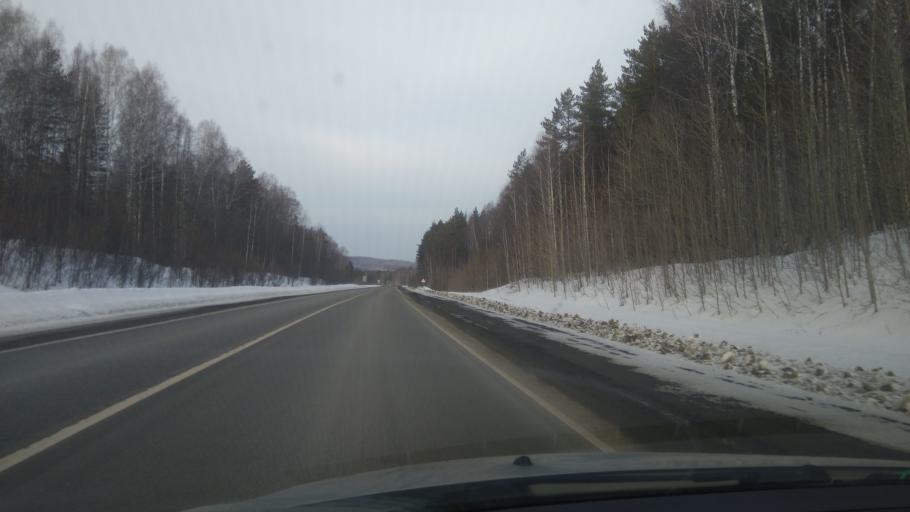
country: RU
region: Sverdlovsk
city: Bisert'
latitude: 56.8354
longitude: 58.8854
